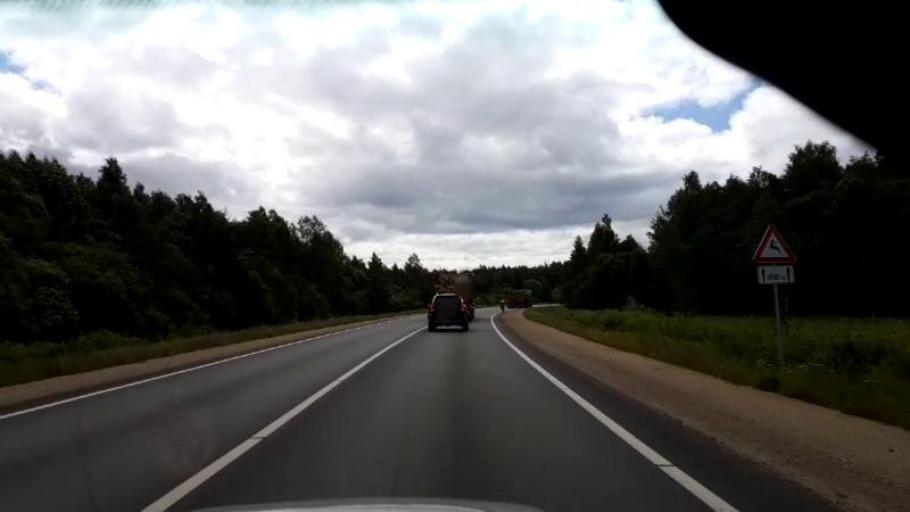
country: LV
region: Salacgrivas
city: Salacgriva
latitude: 57.7293
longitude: 24.3671
